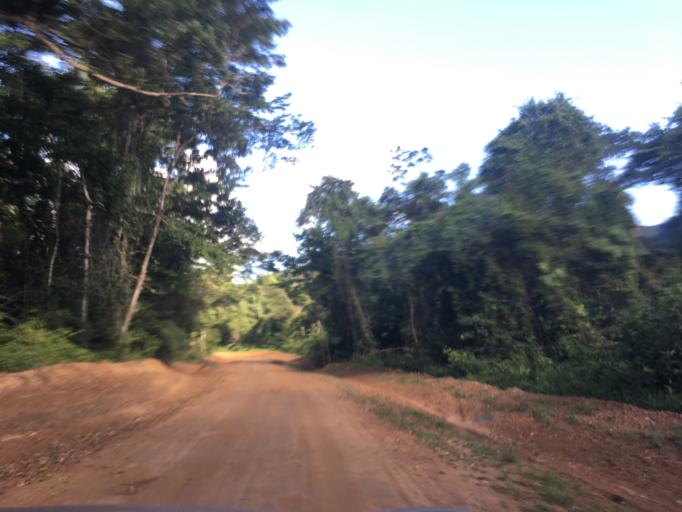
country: BZ
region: Stann Creek
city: Placencia
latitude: 16.7848
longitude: -88.4507
